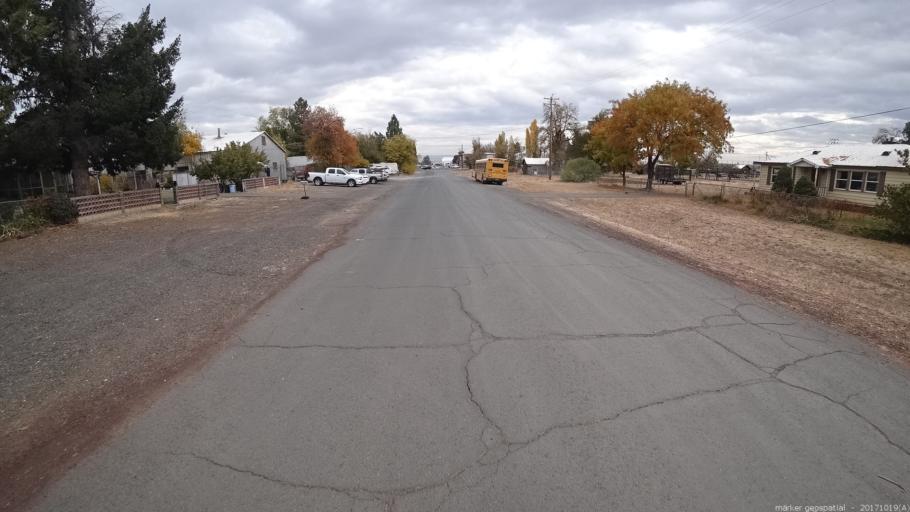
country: US
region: California
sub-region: Shasta County
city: Burney
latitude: 41.0463
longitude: -121.4027
